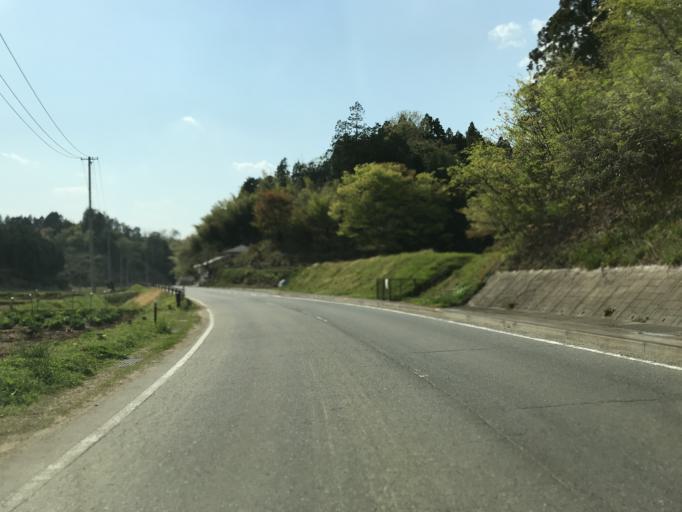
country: JP
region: Fukushima
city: Iwaki
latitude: 37.0023
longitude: 140.7706
